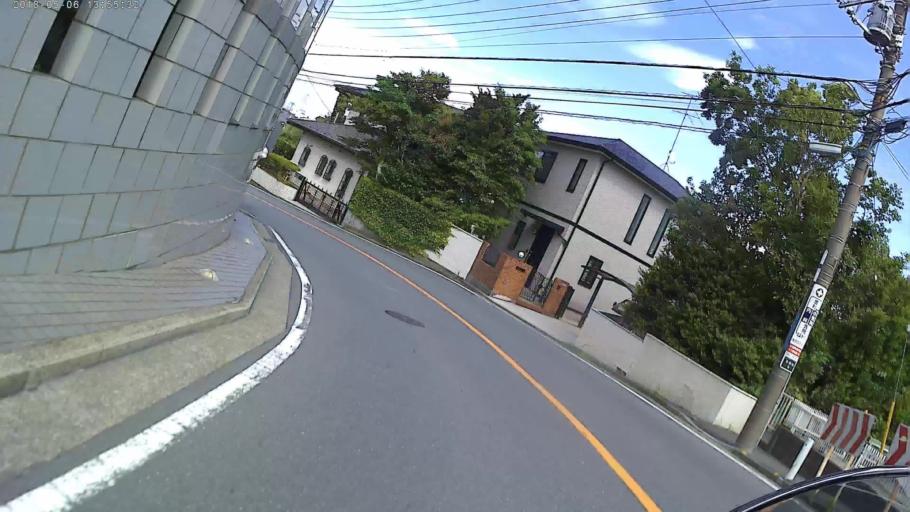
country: JP
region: Kanagawa
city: Yokohama
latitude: 35.4353
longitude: 139.5847
